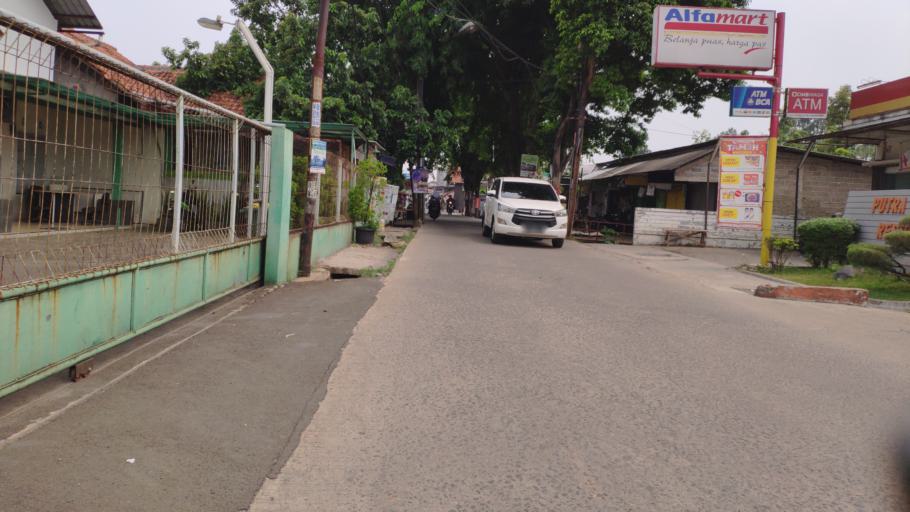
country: ID
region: West Java
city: Depok
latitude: -6.3738
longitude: 106.8009
